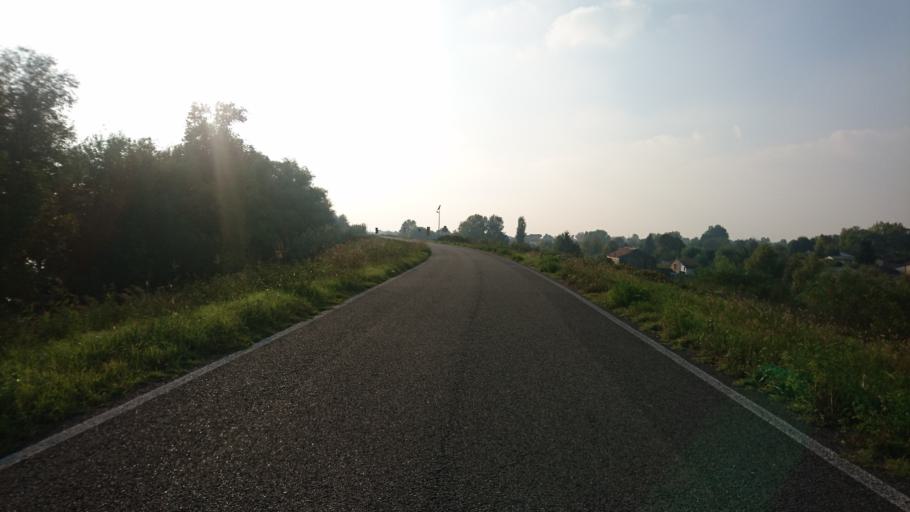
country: IT
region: Veneto
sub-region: Provincia di Rovigo
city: Canaro
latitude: 44.9193
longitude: 11.6849
